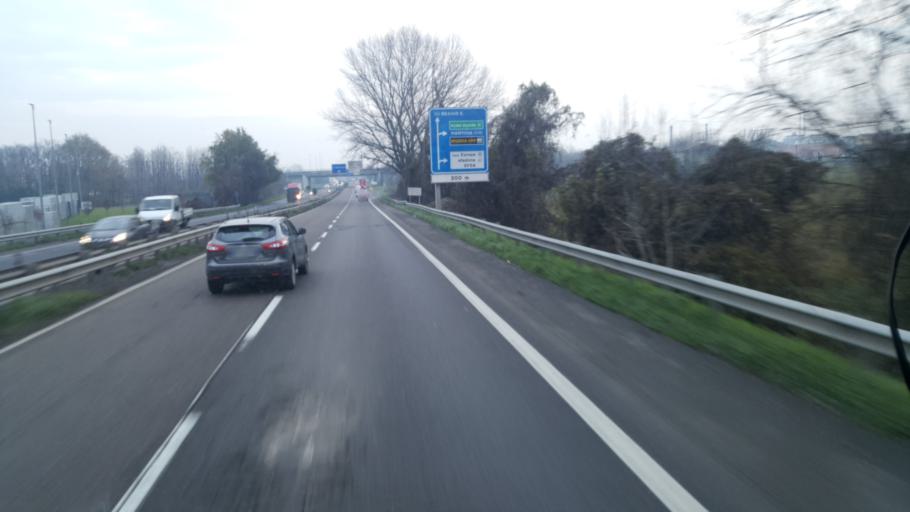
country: IT
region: Emilia-Romagna
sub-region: Provincia di Parma
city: Parma
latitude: 44.8221
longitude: 10.3228
